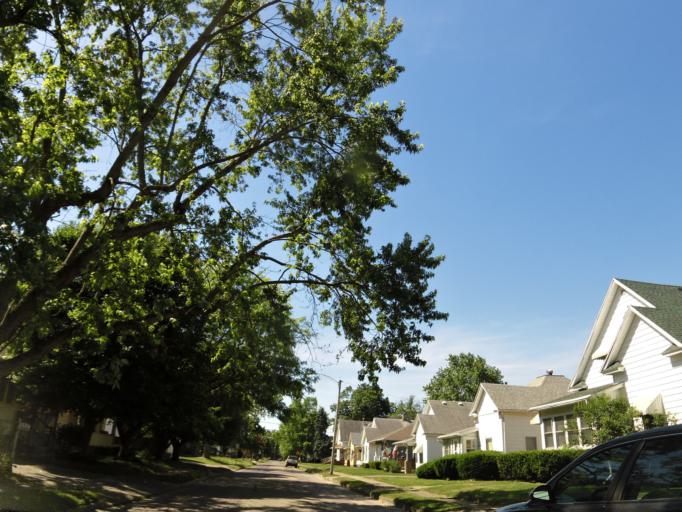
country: US
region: Illinois
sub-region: Vermilion County
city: Danville
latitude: 40.1347
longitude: -87.5981
